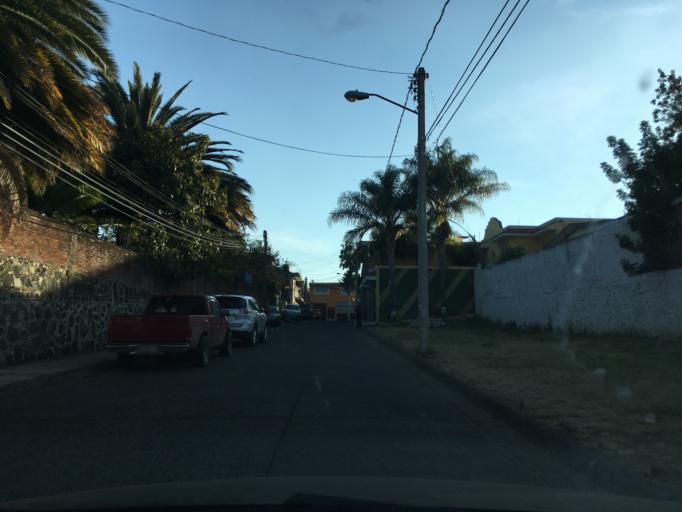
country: MX
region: Michoacan
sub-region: Uruapan
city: Uruapan
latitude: 19.4171
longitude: -102.0698
